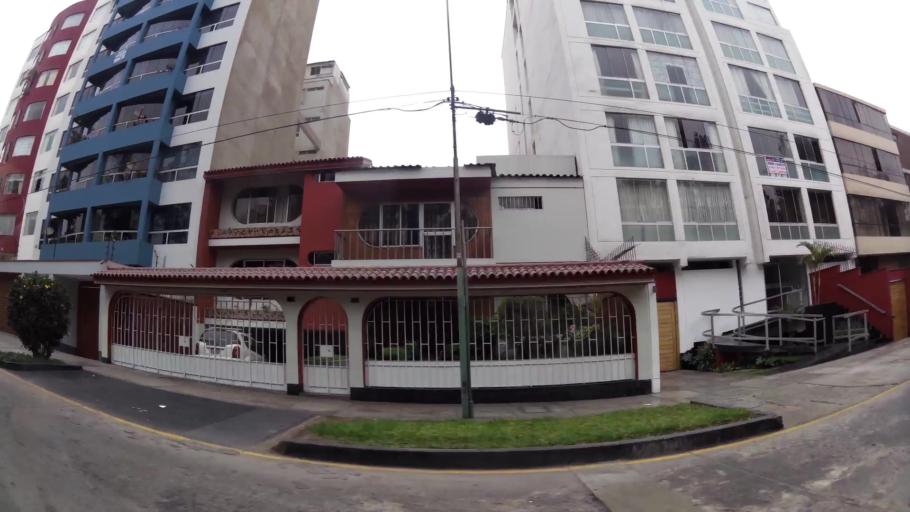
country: PE
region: Lima
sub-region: Lima
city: San Luis
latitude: -12.0932
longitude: -76.9966
